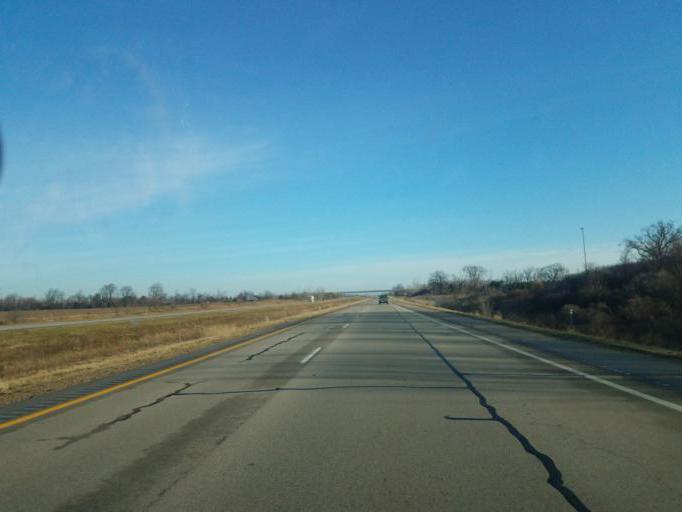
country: US
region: Michigan
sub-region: Clinton County
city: Saint Johns
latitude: 42.9363
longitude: -84.5184
